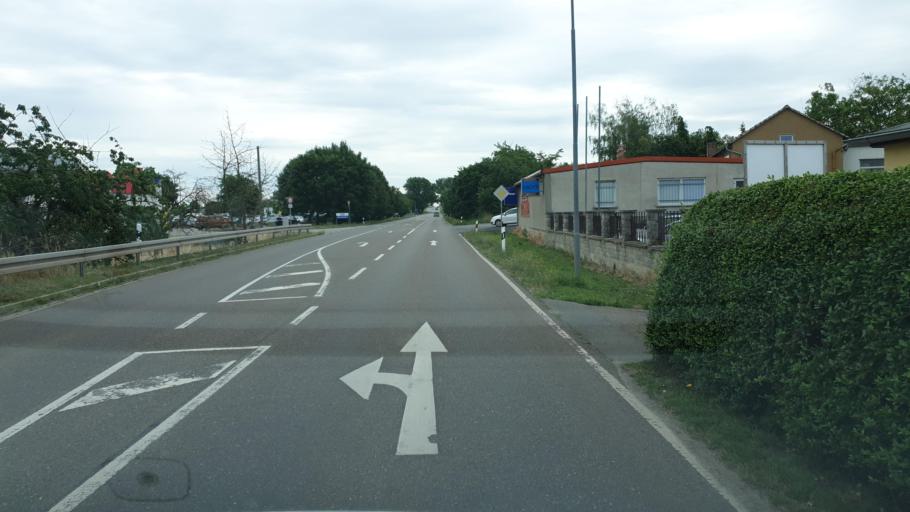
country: DE
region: Saxony-Anhalt
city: Querfurt
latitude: 51.3735
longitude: 11.6008
